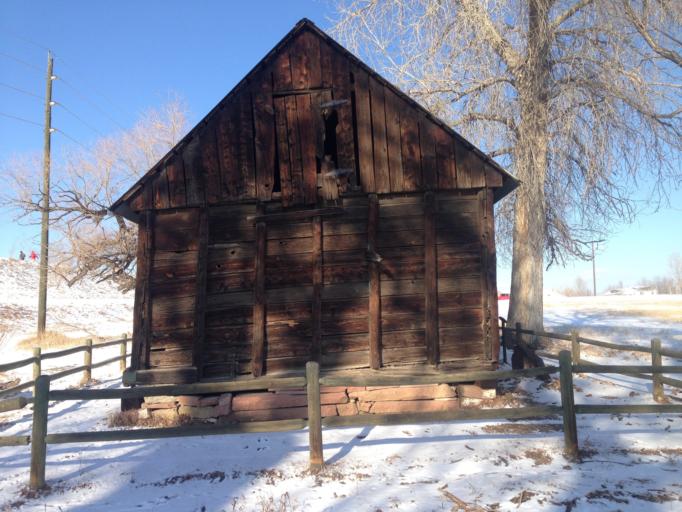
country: US
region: Colorado
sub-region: Boulder County
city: Lafayette
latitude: 39.9930
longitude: -105.1091
